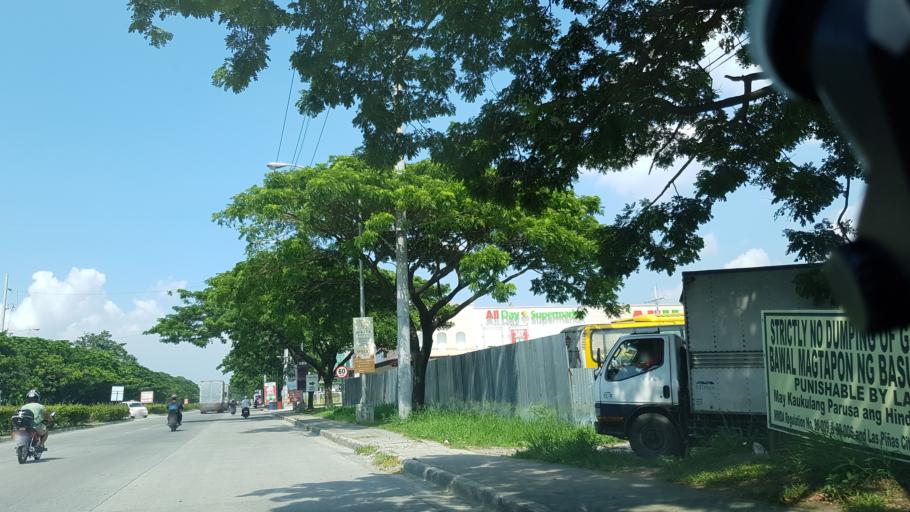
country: PH
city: Sambayanihan People's Village
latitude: 14.4762
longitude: 120.9830
